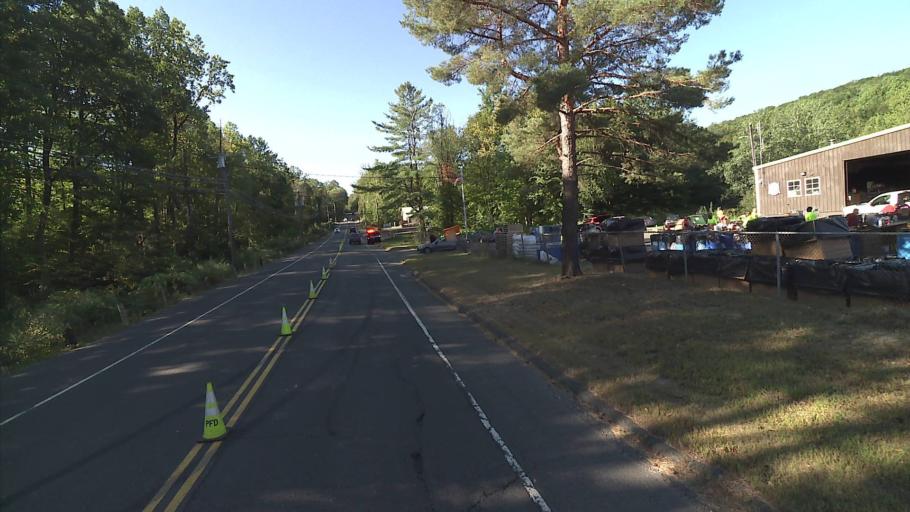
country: US
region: Connecticut
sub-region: New Haven County
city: Prospect
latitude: 41.5073
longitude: -72.9465
